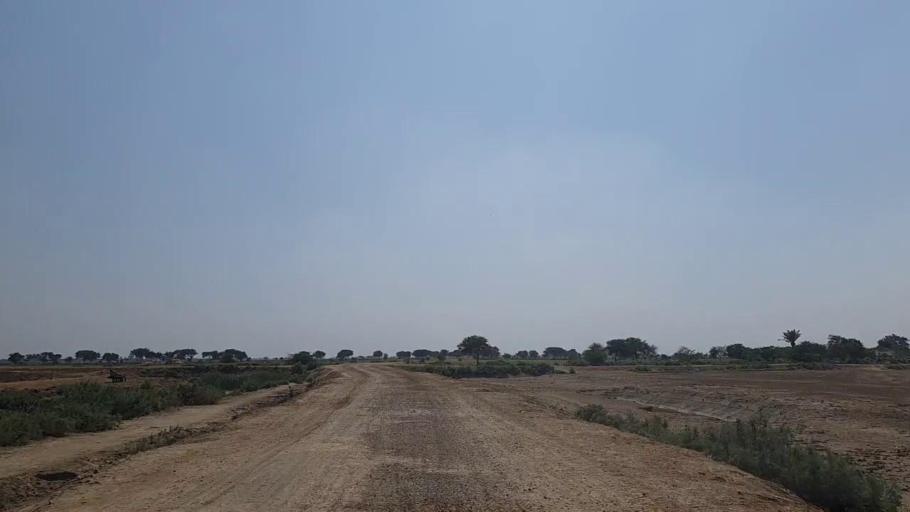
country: PK
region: Sindh
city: Jati
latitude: 24.5375
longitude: 68.3152
